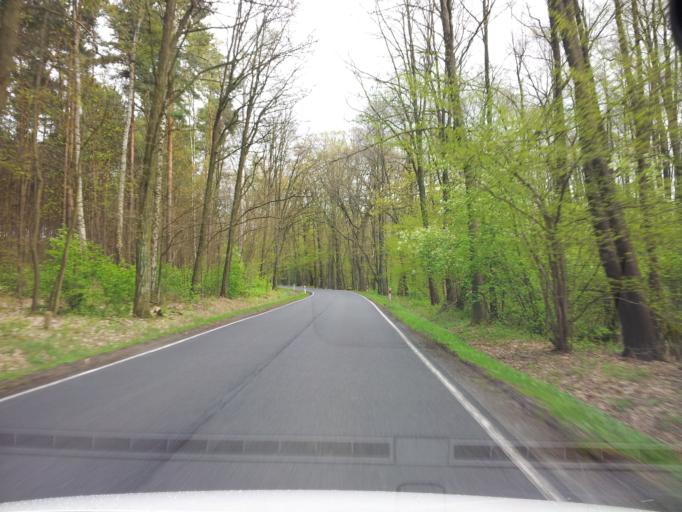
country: PL
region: Lubusz
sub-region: Powiat zielonogorski
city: Ochla
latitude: 51.8712
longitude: 15.5217
